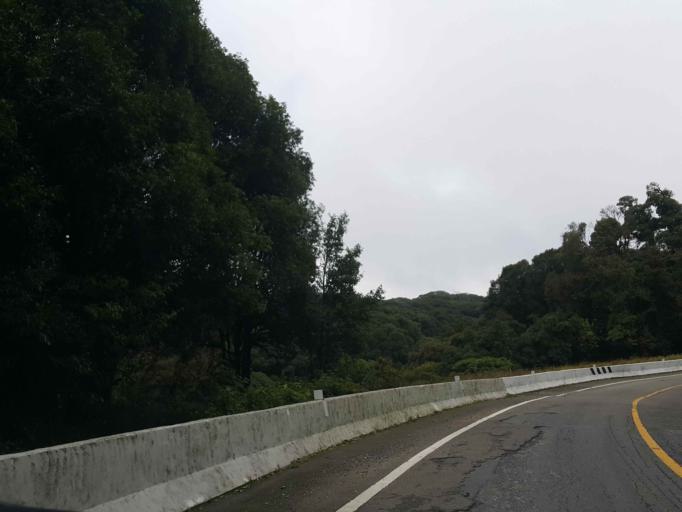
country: TH
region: Chiang Mai
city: Mae Chaem
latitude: 18.5870
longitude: 98.4848
